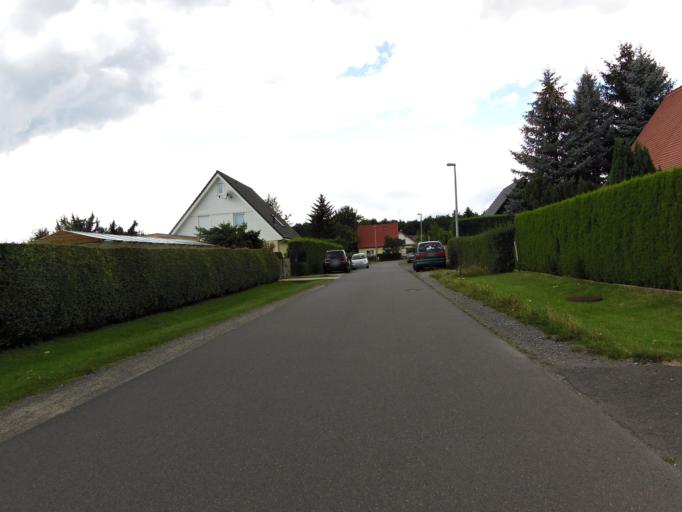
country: DE
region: Saxony
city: Rackwitz
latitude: 51.3865
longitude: 12.4116
